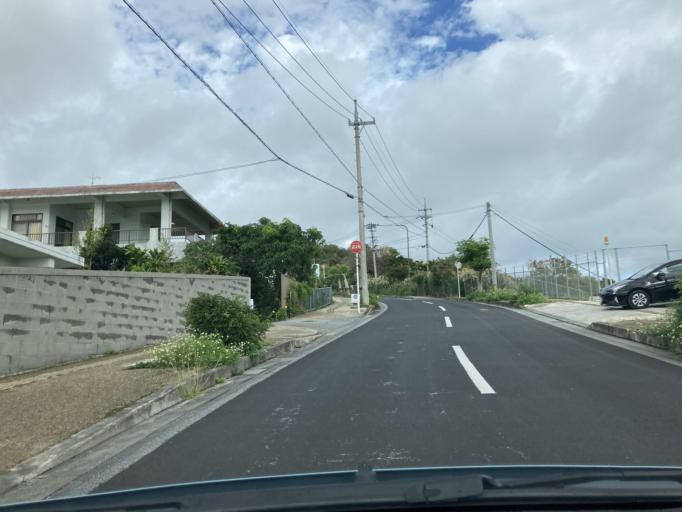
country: JP
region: Okinawa
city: Tomigusuku
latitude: 26.1737
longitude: 127.7441
